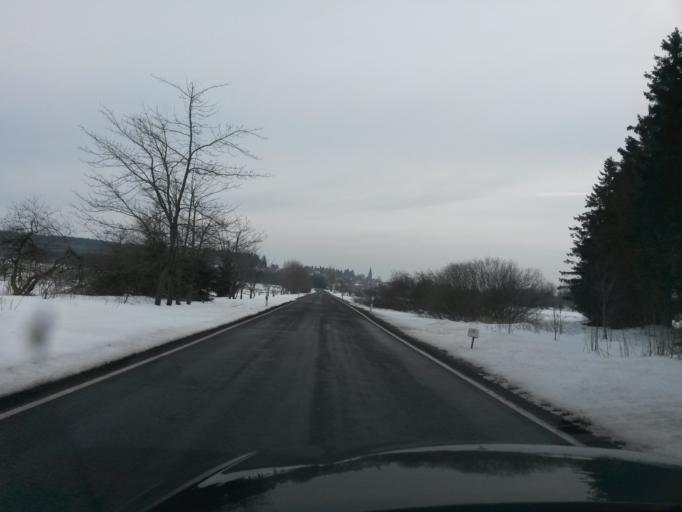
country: DE
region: Thuringia
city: Frankenheim
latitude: 50.5473
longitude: 10.0553
